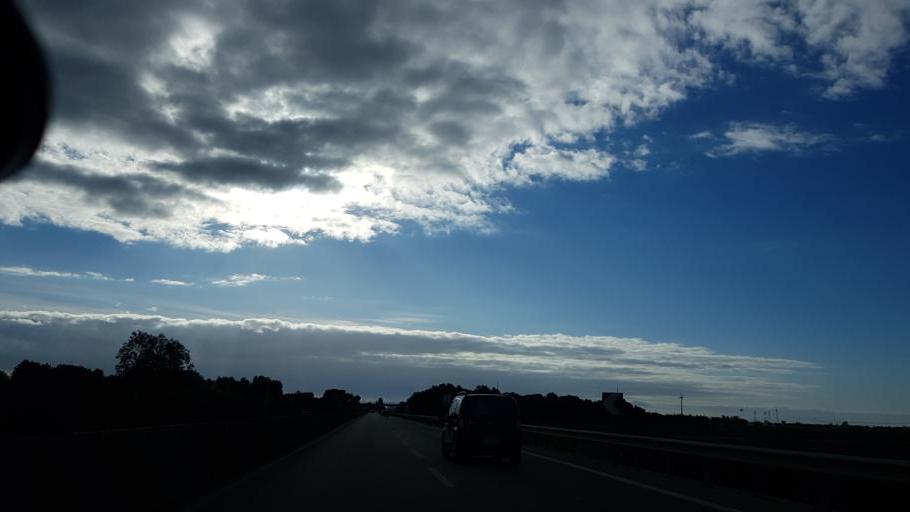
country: IT
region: Apulia
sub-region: Provincia di Brindisi
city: La Rosa
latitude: 40.5829
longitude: 17.9764
